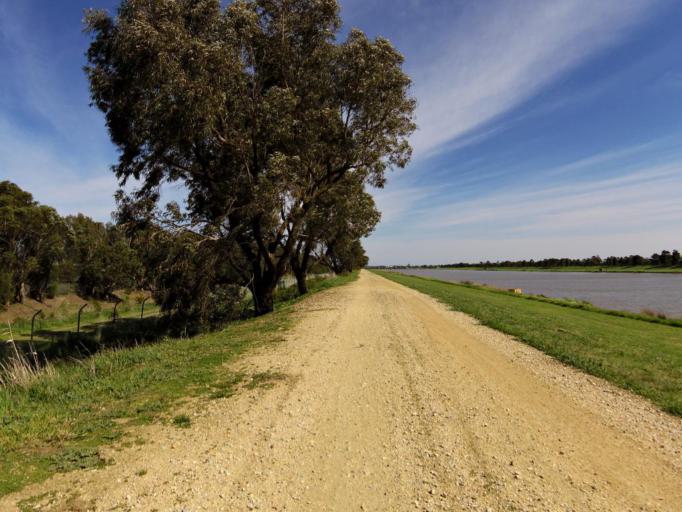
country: AU
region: Victoria
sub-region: Kingston
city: Patterson Lakes
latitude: -38.0508
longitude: 145.1639
